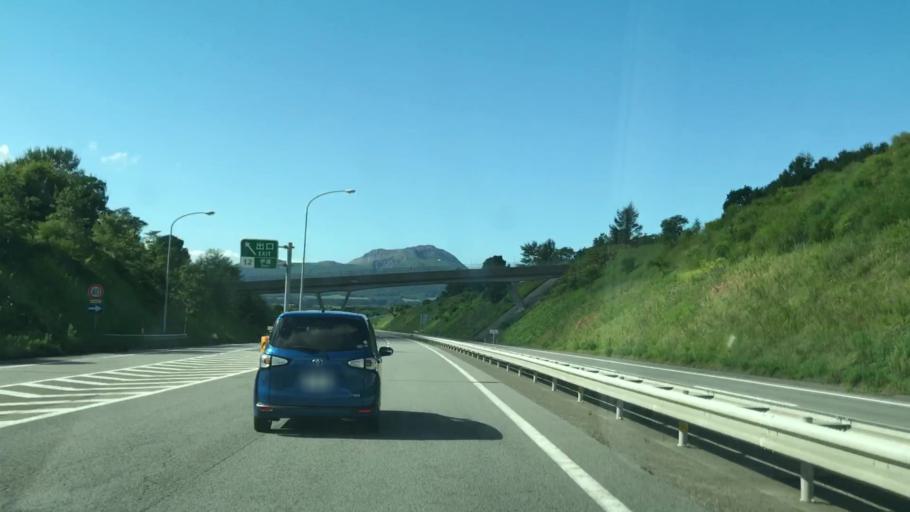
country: JP
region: Hokkaido
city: Date
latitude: 42.4801
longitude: 140.8989
